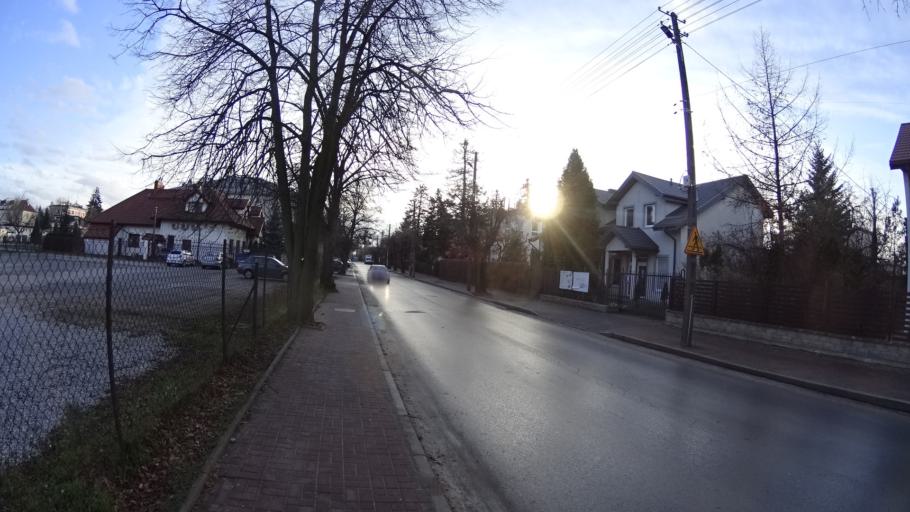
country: PL
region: Masovian Voivodeship
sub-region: Powiat warszawski zachodni
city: Ozarow Mazowiecki
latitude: 52.2099
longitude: 20.7962
